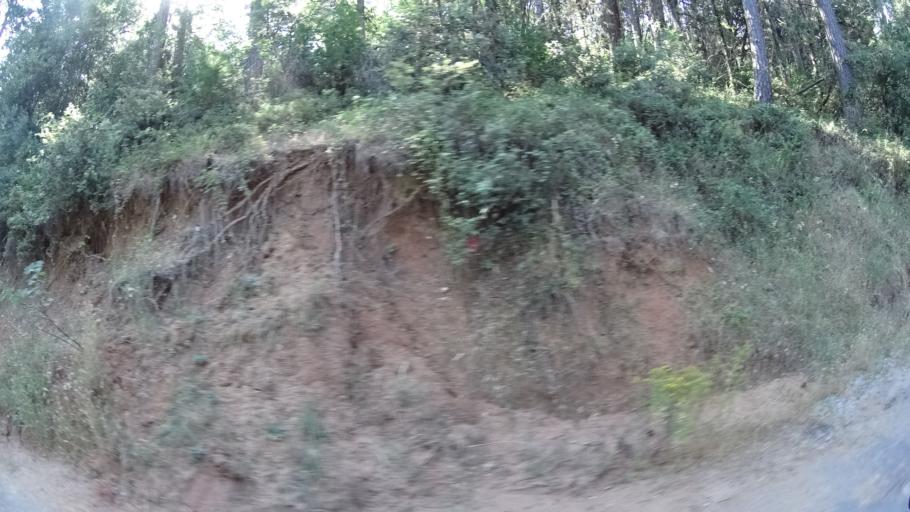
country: US
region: California
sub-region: Amador County
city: Pioneer
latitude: 38.4104
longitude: -120.5576
